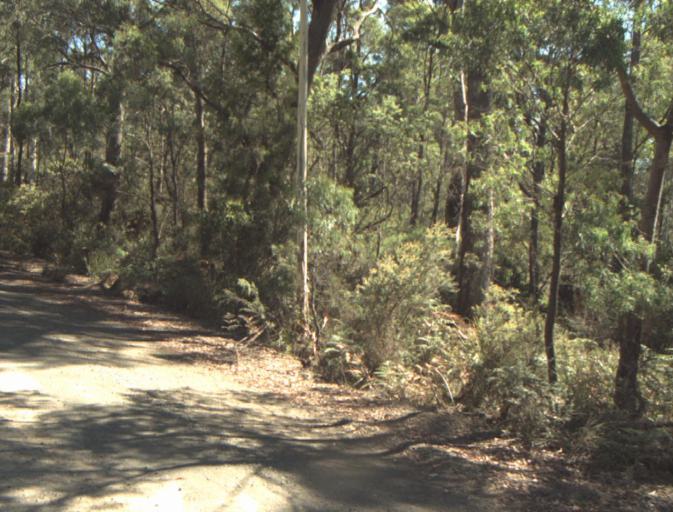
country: AU
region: Tasmania
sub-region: Launceston
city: Mayfield
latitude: -41.3428
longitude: 147.2122
